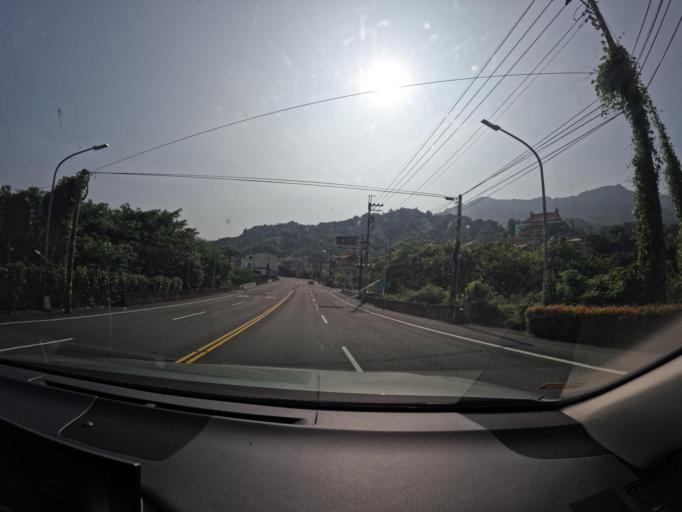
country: TW
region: Taiwan
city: Yujing
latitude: 23.0695
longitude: 120.5134
